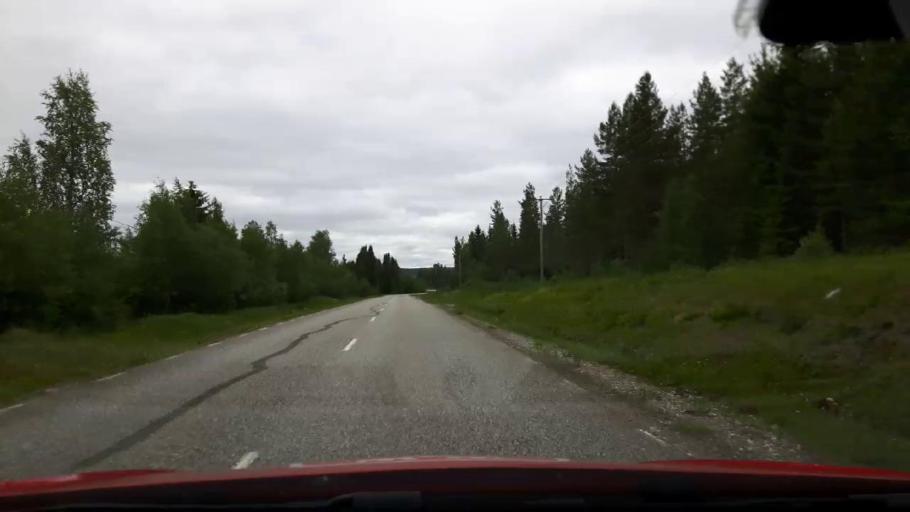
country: SE
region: Jaemtland
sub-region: Stroemsunds Kommun
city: Stroemsund
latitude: 63.3146
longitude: 15.7624
